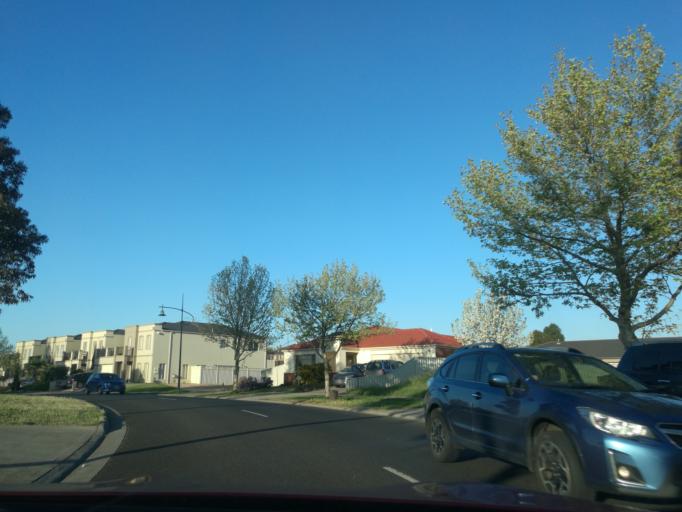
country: AU
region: Victoria
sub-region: Wyndham
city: Williams Landing
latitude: -37.8880
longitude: 144.7405
